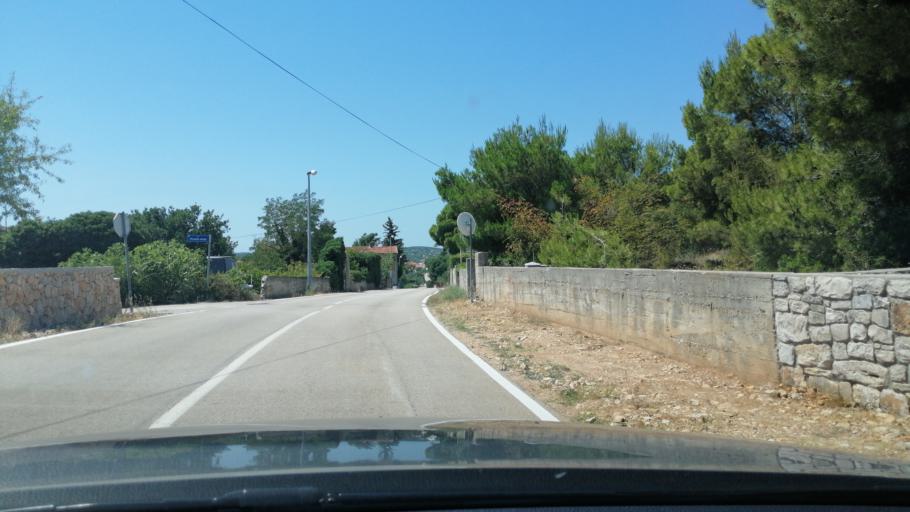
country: HR
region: Sibensko-Kniniska
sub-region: Grad Sibenik
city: Pirovac
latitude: 43.8230
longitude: 15.6758
